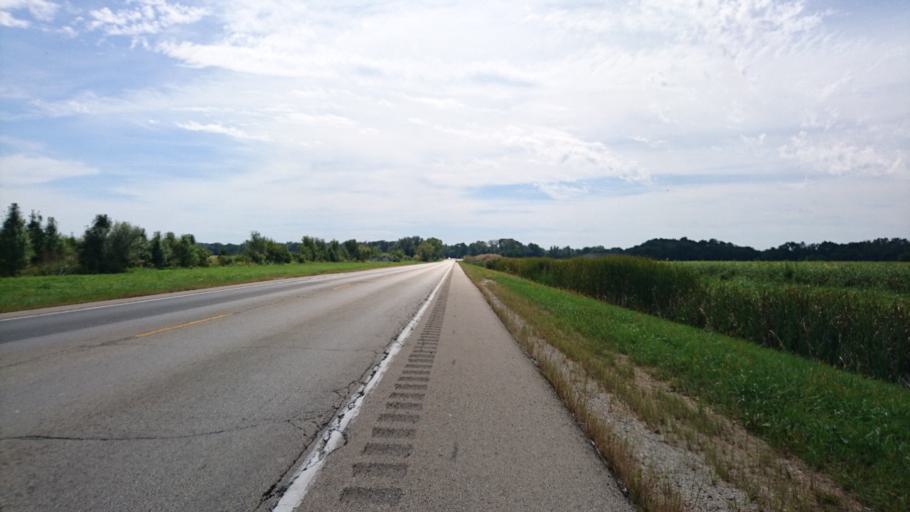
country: US
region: Illinois
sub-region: Will County
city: Wilmington
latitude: 41.3169
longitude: -88.1325
